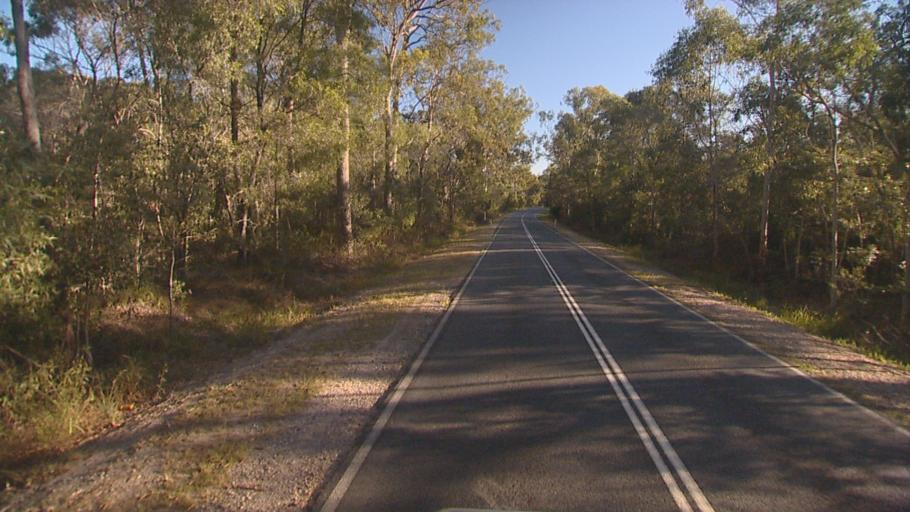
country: AU
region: Queensland
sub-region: Logan
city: Chambers Flat
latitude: -27.7780
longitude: 153.0739
